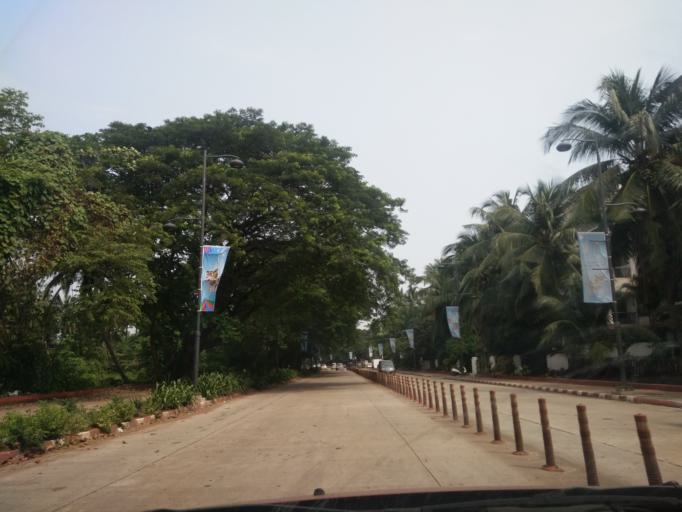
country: IN
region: Goa
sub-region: North Goa
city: Taleigao
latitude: 15.4645
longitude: 73.8056
